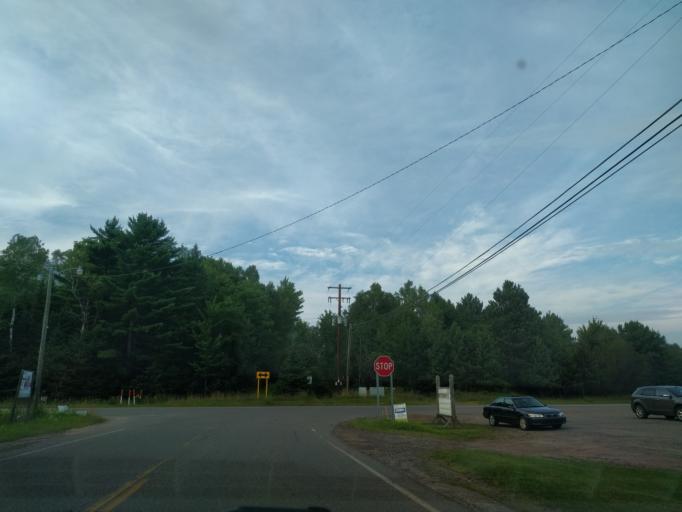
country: US
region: Michigan
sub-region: Marquette County
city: Gwinn
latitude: 46.2830
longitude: -87.4684
